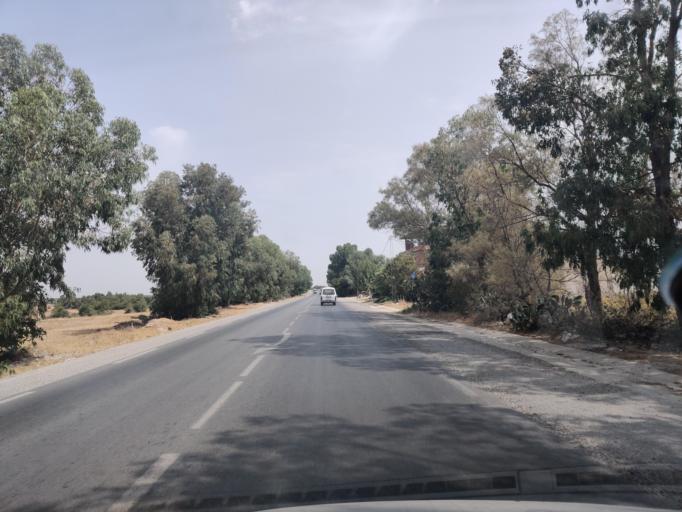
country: TN
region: Nabul
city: Al Hammamat
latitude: 36.4621
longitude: 10.5709
